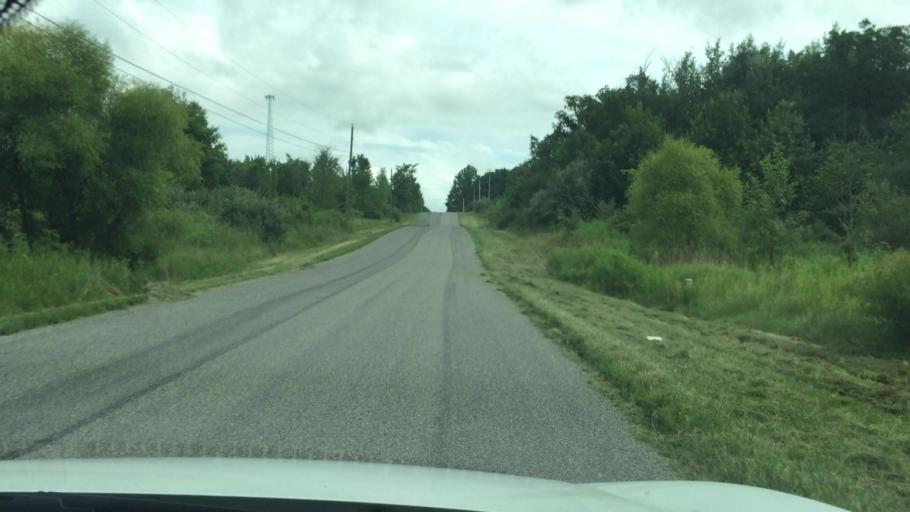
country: US
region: Ohio
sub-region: Champaign County
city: North Lewisburg
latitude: 40.2635
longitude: -83.5352
